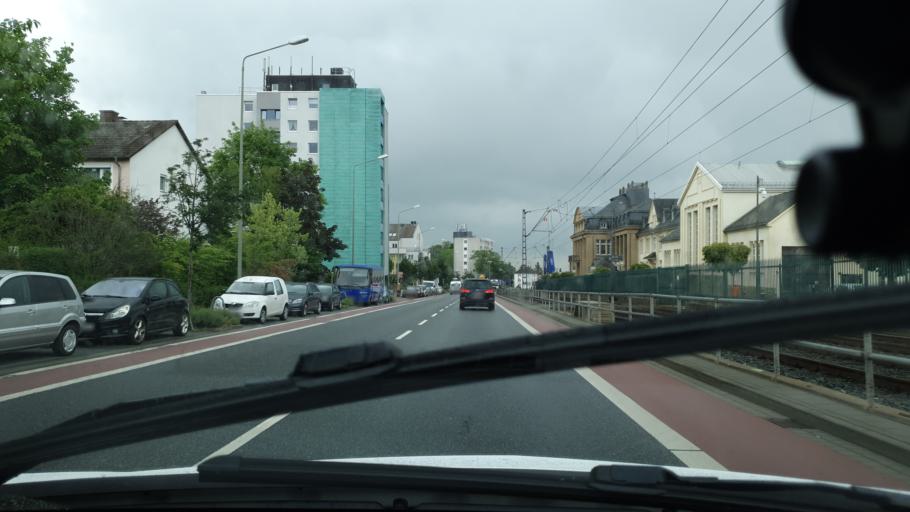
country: DE
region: Hesse
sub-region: Regierungsbezirk Darmstadt
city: Oberursel
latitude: 50.2122
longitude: 8.5662
